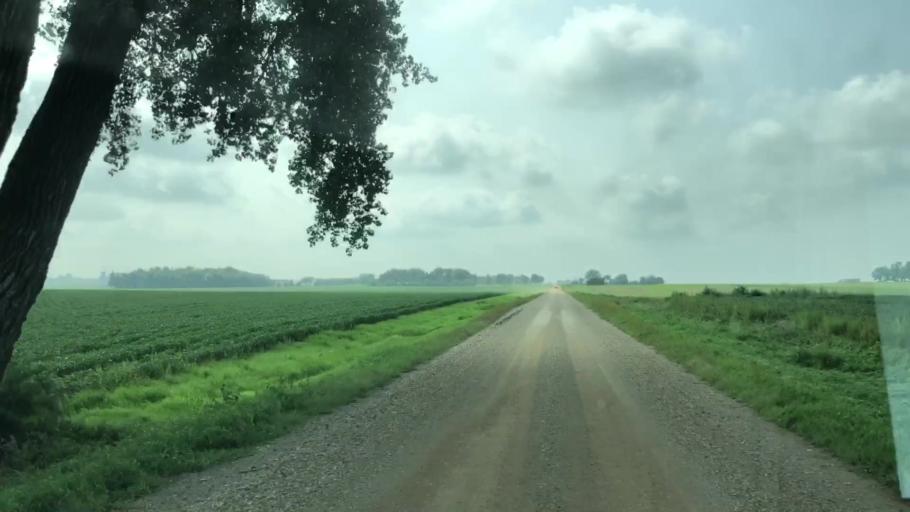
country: US
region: Iowa
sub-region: O'Brien County
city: Sheldon
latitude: 43.1942
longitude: -95.8822
